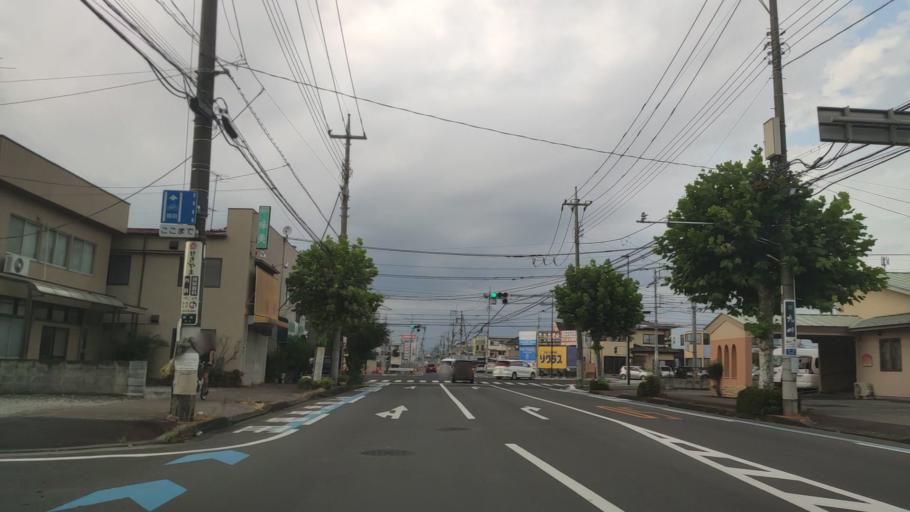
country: JP
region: Tochigi
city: Utsunomiya-shi
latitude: 36.5505
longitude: 139.8756
